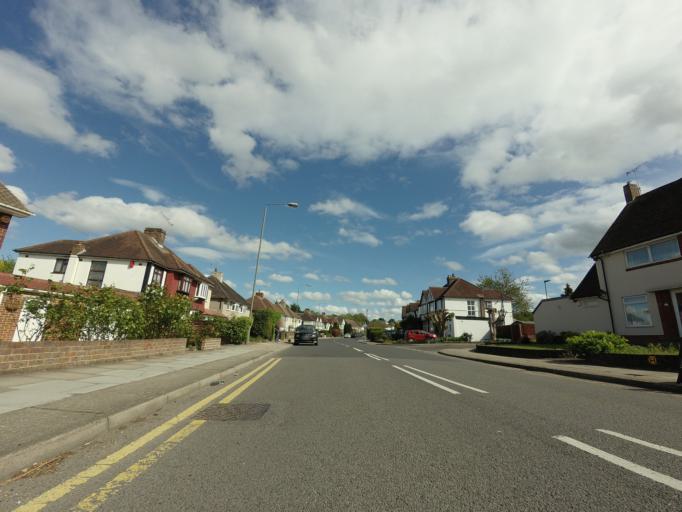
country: GB
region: England
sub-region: Greater London
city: Orpington
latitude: 51.3720
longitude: 0.1113
